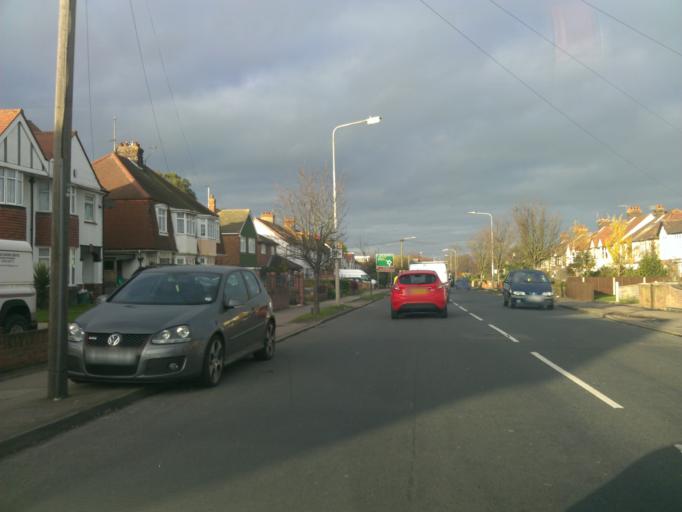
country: GB
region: England
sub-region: Essex
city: Clacton-on-Sea
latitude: 51.8017
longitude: 1.1481
